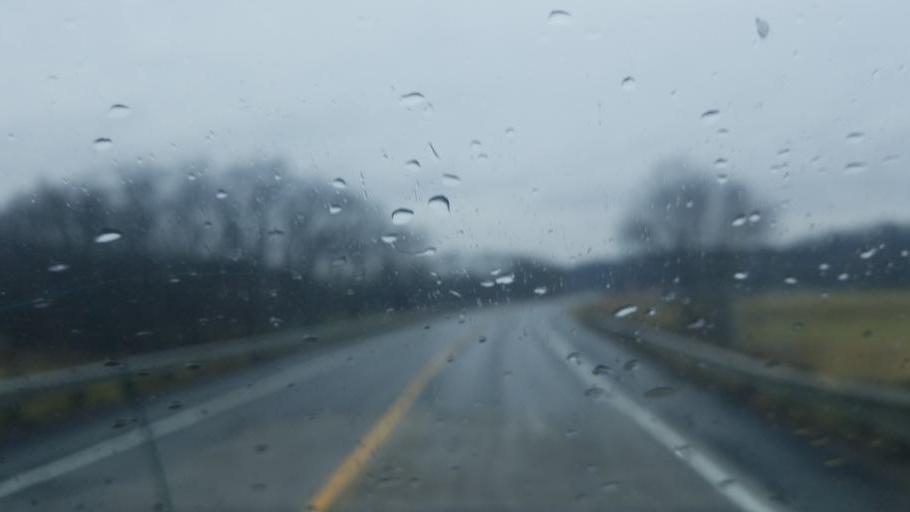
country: US
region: Indiana
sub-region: Brown County
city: Nashville
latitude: 39.1918
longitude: -86.1967
